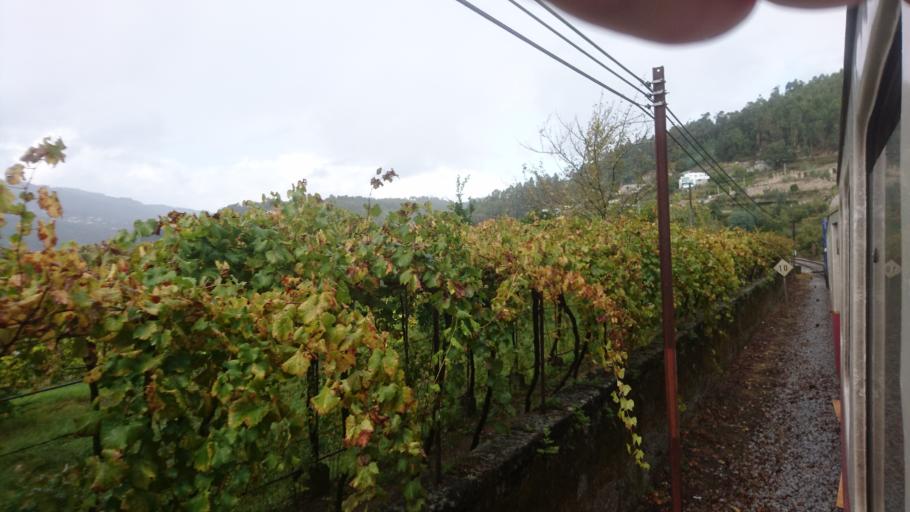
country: PT
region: Viseu
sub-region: Cinfaes
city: Cinfaes
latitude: 41.0975
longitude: -8.0817
